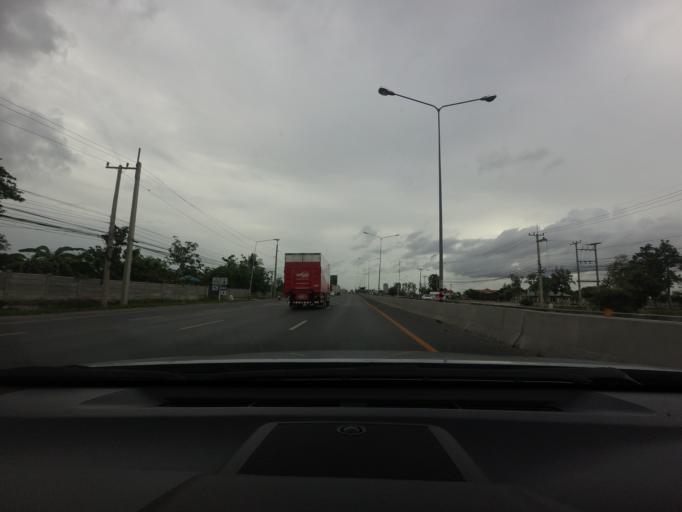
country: TH
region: Phetchaburi
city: Tha Yang
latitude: 12.8753
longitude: 99.9151
